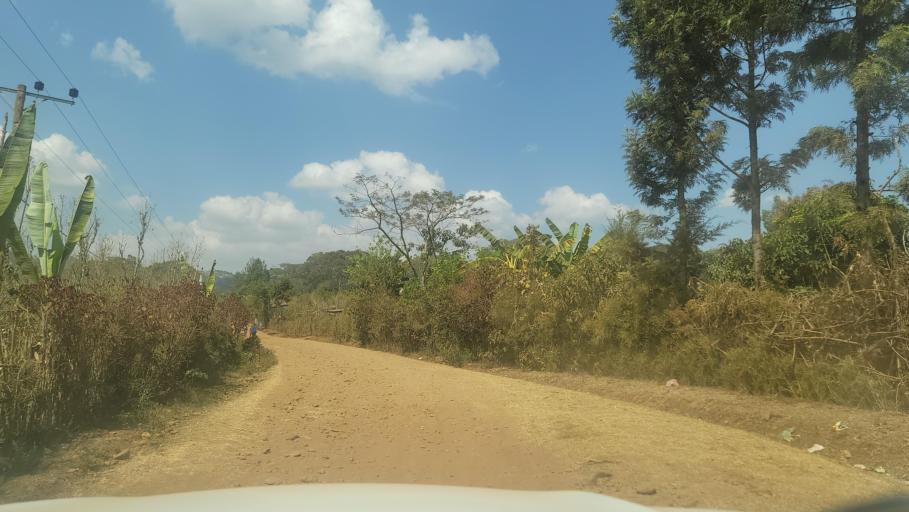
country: ET
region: Oromiya
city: Agaro
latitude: 7.8395
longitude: 36.5350
